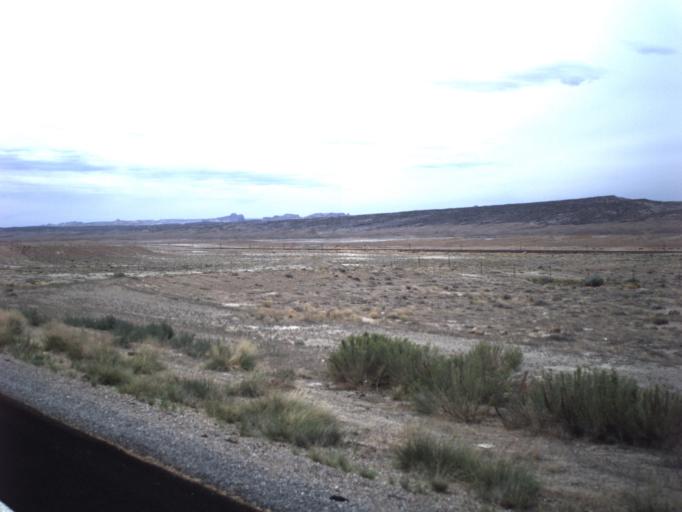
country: US
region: Utah
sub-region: Carbon County
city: East Carbon City
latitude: 39.1852
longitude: -110.3385
